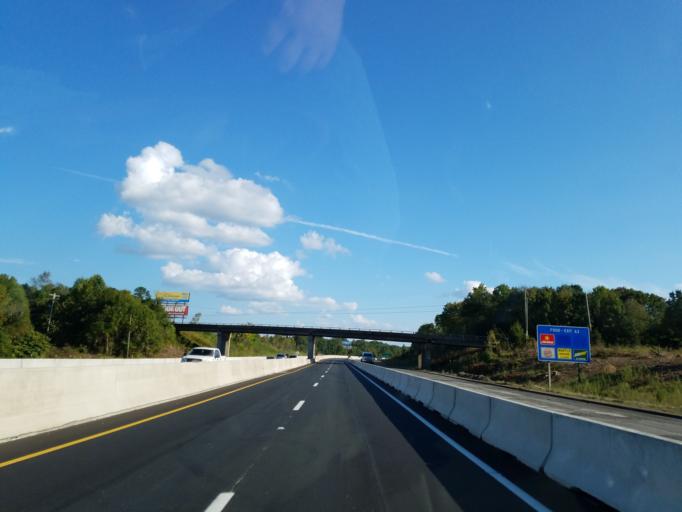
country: US
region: North Carolina
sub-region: Rowan County
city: Landis
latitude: 35.5103
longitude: -80.5656
